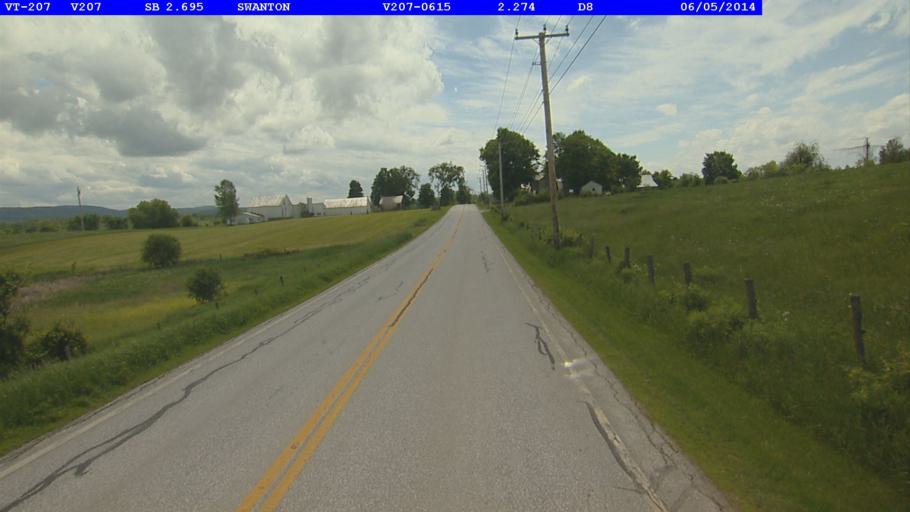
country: US
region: Vermont
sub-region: Franklin County
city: Swanton
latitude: 44.8773
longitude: -73.0713
